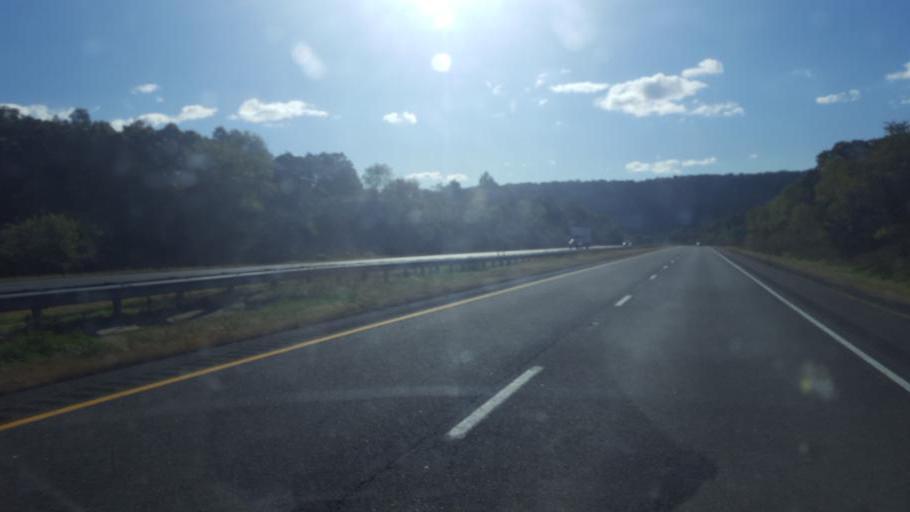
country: US
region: Maryland
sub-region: Washington County
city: Hancock
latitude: 39.7037
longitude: -78.2575
